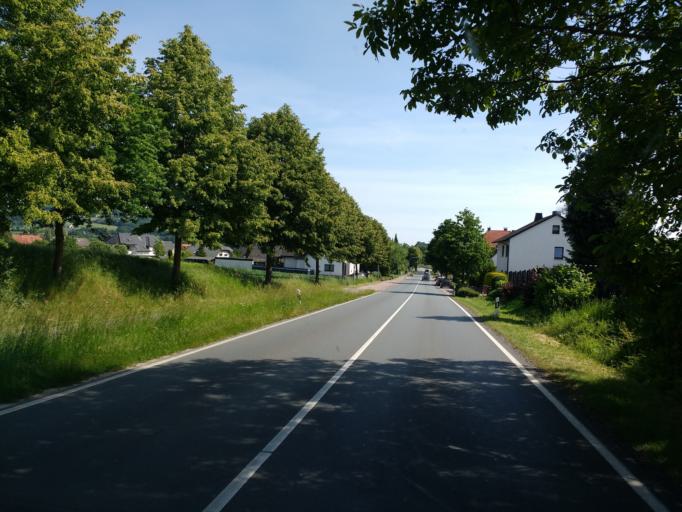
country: DE
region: North Rhine-Westphalia
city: Loehne
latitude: 52.1648
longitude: 8.6633
